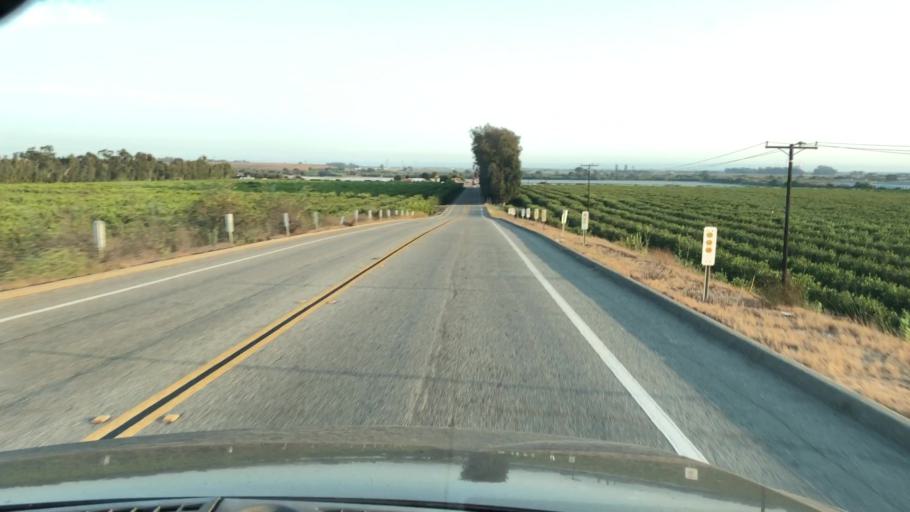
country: US
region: California
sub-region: Ventura County
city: Oxnard Shores
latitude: 34.2503
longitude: -119.2345
